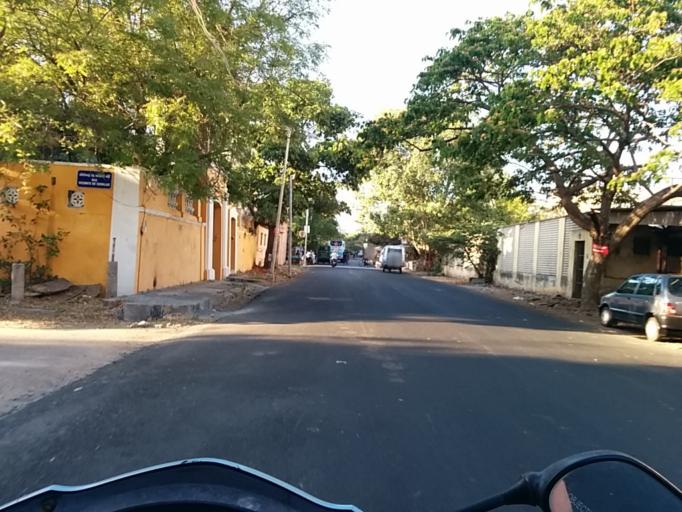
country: IN
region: Pondicherry
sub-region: Puducherry
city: Puducherry
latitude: 11.9321
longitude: 79.8321
